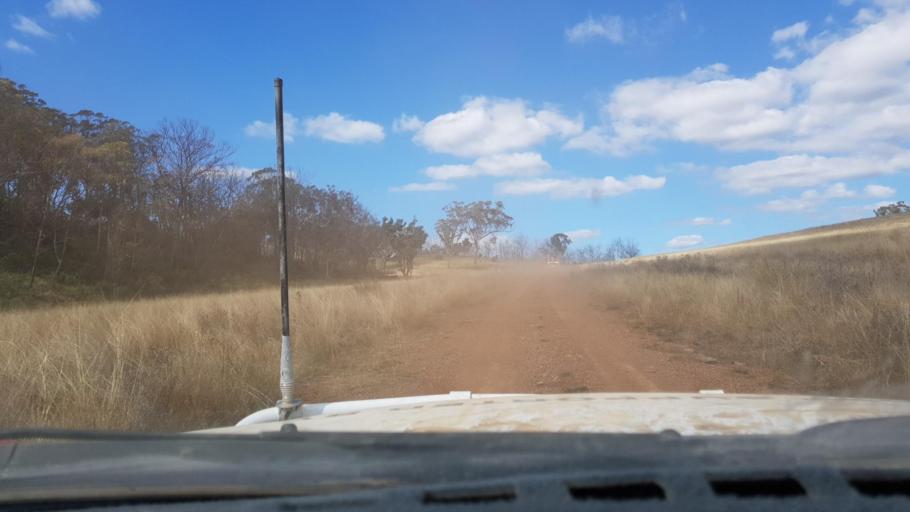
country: AU
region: New South Wales
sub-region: Tamworth Municipality
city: Manilla
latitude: -30.4347
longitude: 150.8261
